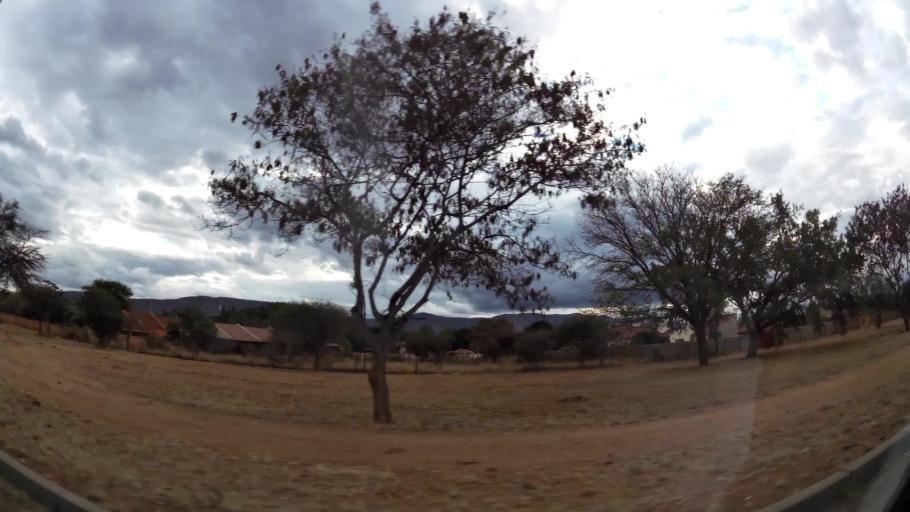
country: ZA
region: Limpopo
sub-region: Waterberg District Municipality
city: Mokopane
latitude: -24.2095
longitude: 29.0060
